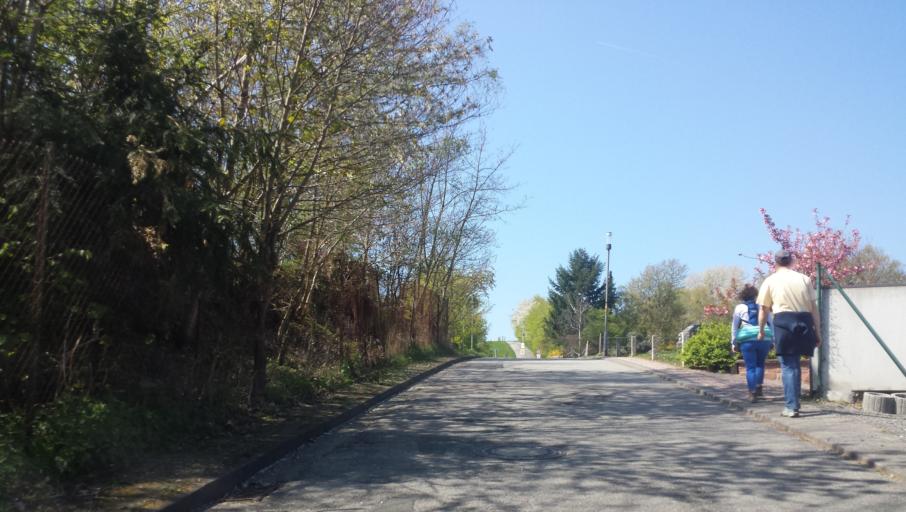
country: DE
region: Hesse
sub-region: Regierungsbezirk Darmstadt
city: Morlenbach
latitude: 49.6278
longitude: 8.7246
